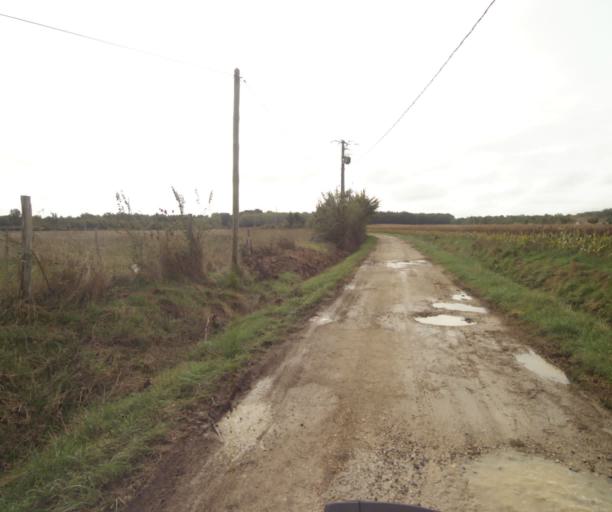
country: FR
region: Midi-Pyrenees
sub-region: Departement du Tarn-et-Garonne
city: Campsas
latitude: 43.9203
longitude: 1.2965
